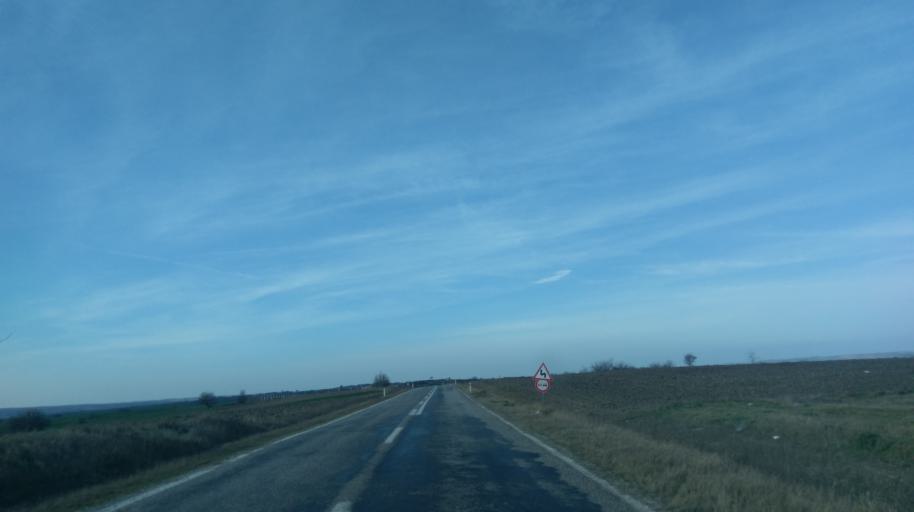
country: TR
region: Kirklareli
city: Pehlivankoy
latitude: 41.3223
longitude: 26.8738
